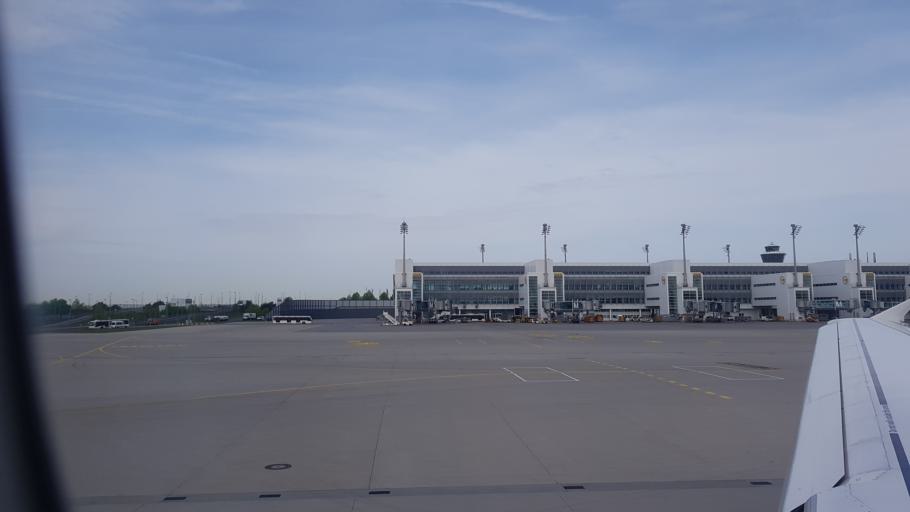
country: DE
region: Bavaria
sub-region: Upper Bavaria
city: Hallbergmoos
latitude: 48.3501
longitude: 11.7965
